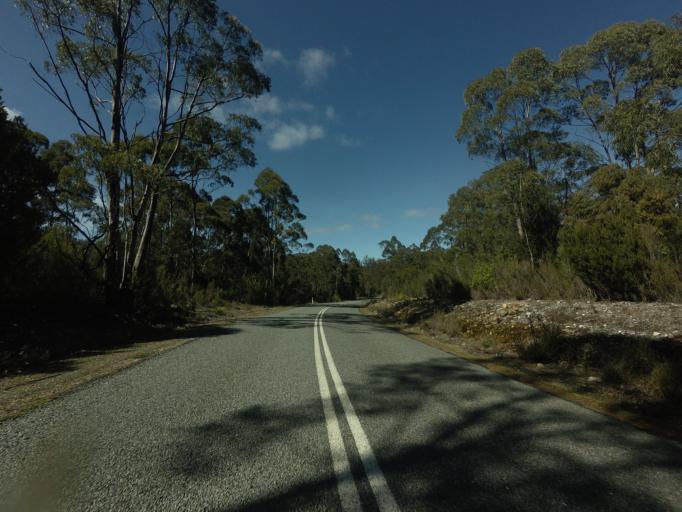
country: AU
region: Tasmania
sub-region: Huon Valley
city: Geeveston
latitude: -42.7731
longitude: 146.3977
